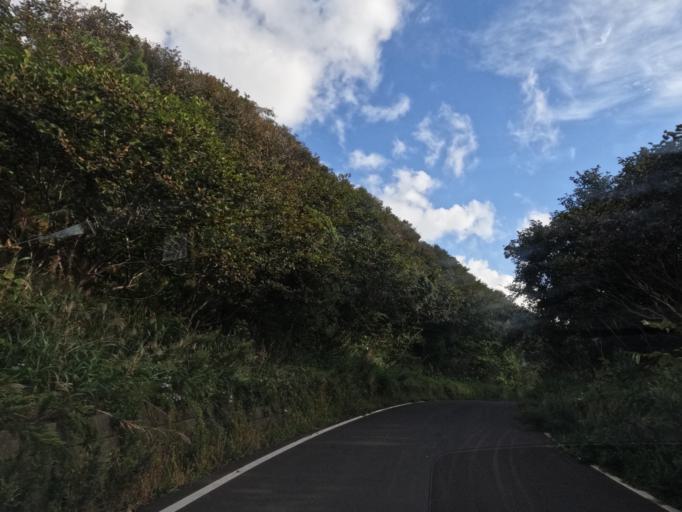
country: JP
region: Hokkaido
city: Muroran
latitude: 42.3077
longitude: 141.0056
